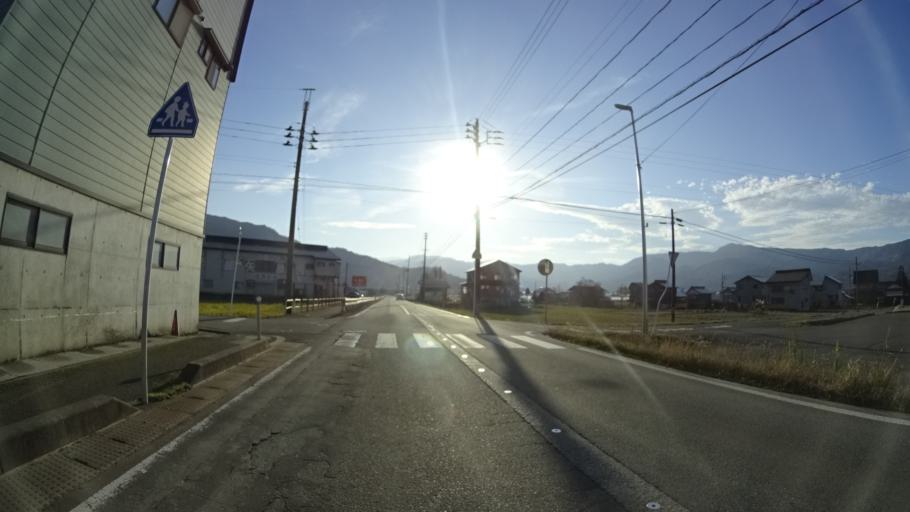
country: JP
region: Niigata
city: Shiozawa
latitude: 37.0151
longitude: 138.8564
